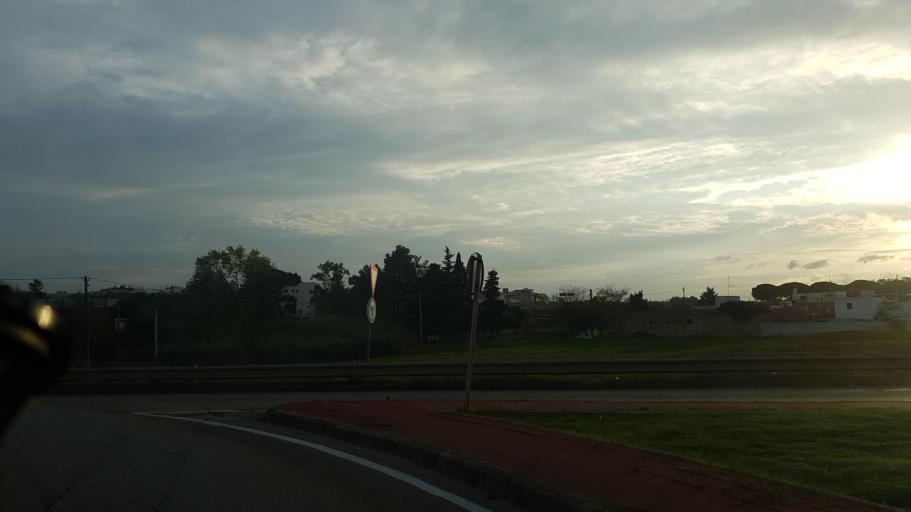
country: IT
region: Apulia
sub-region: Provincia di Brindisi
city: Latiano
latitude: 40.5601
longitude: 17.7146
